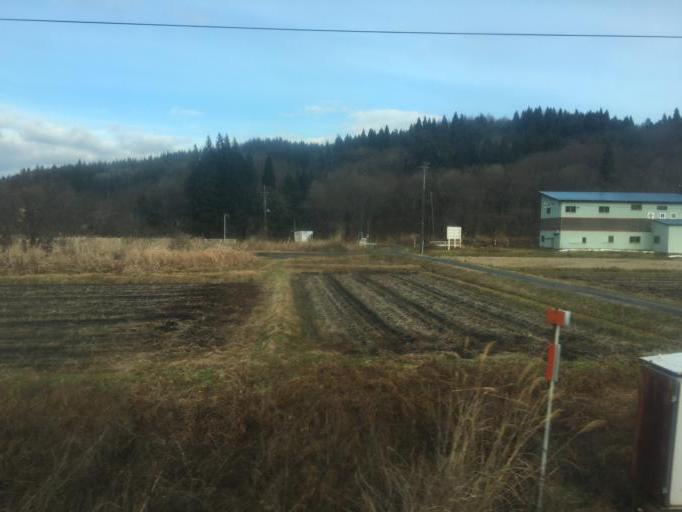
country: JP
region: Akita
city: Takanosu
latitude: 40.2629
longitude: 140.4281
